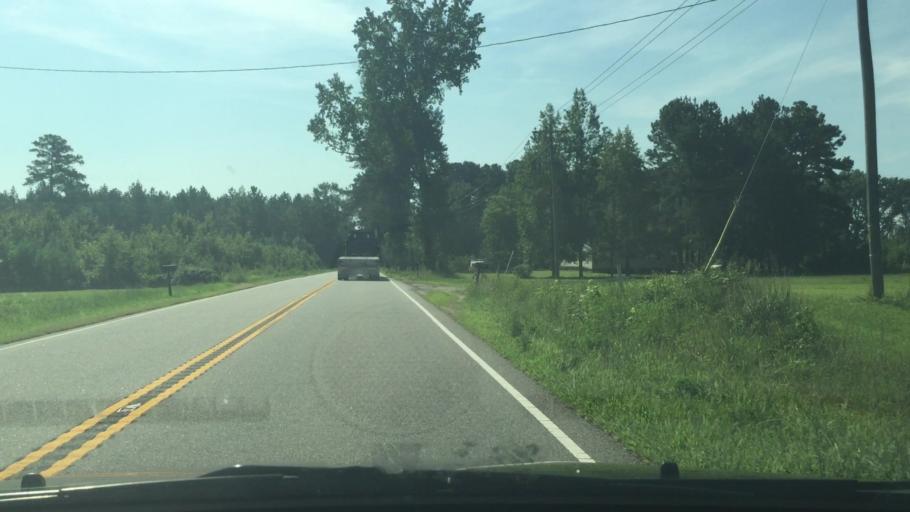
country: US
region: Virginia
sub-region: Sussex County
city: Sussex
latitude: 37.0253
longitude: -77.2914
